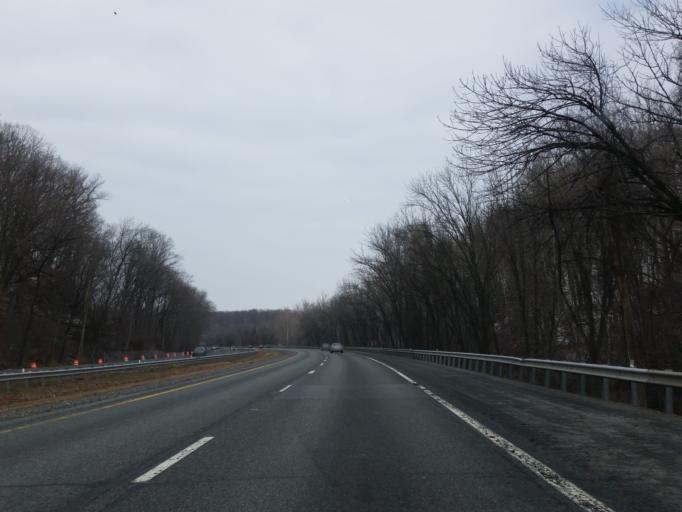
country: US
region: Maryland
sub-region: Baltimore County
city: Hunt Valley
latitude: 39.5567
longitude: -76.6649
